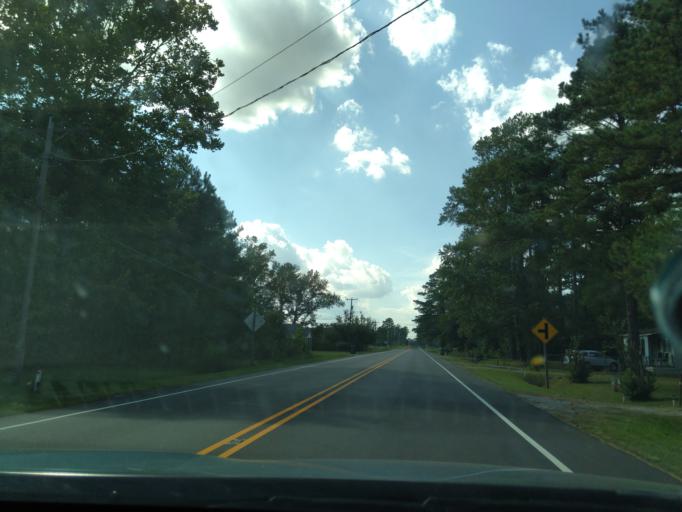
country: US
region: North Carolina
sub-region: Martin County
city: Robersonville
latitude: 35.8235
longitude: -77.3130
